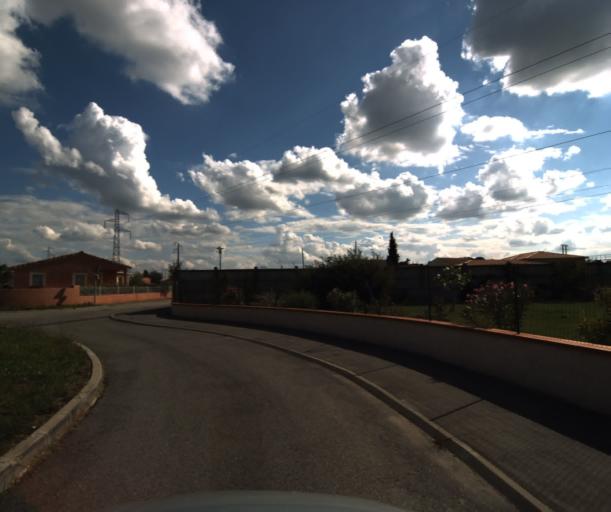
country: FR
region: Midi-Pyrenees
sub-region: Departement de la Haute-Garonne
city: Saubens
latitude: 43.4800
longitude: 1.3555
